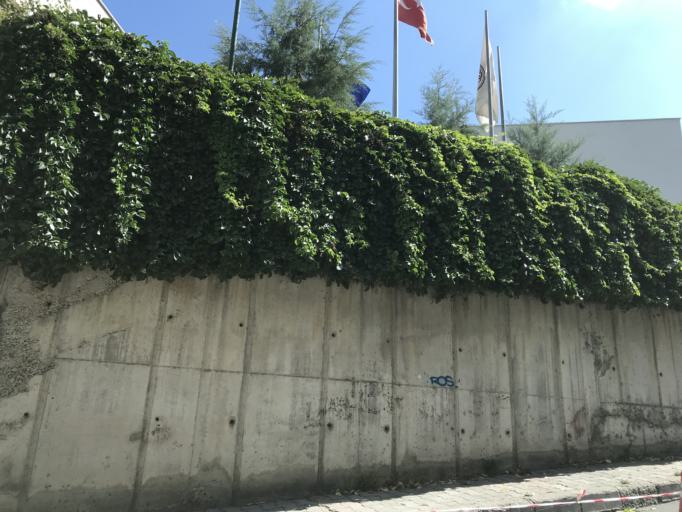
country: TR
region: Ankara
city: Ankara
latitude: 39.9341
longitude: 32.8581
